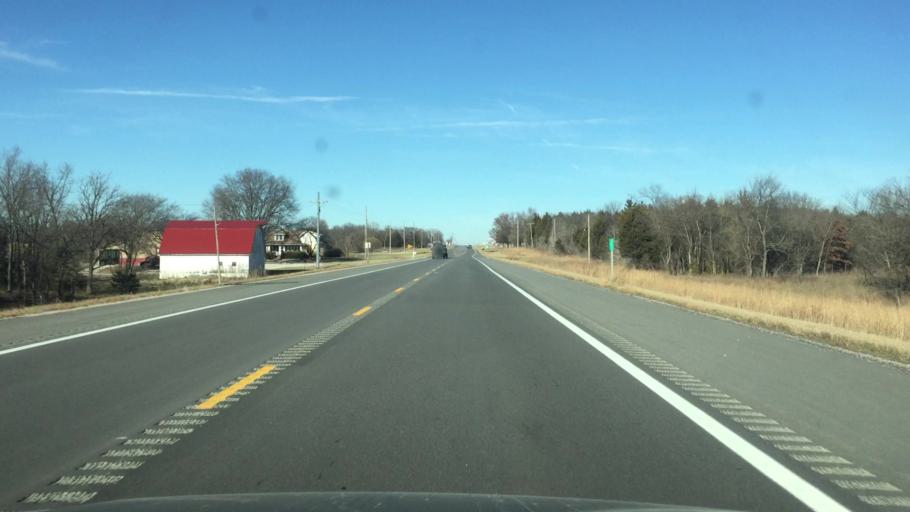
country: US
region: Kansas
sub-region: Franklin County
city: Ottawa
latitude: 38.4816
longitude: -95.2674
